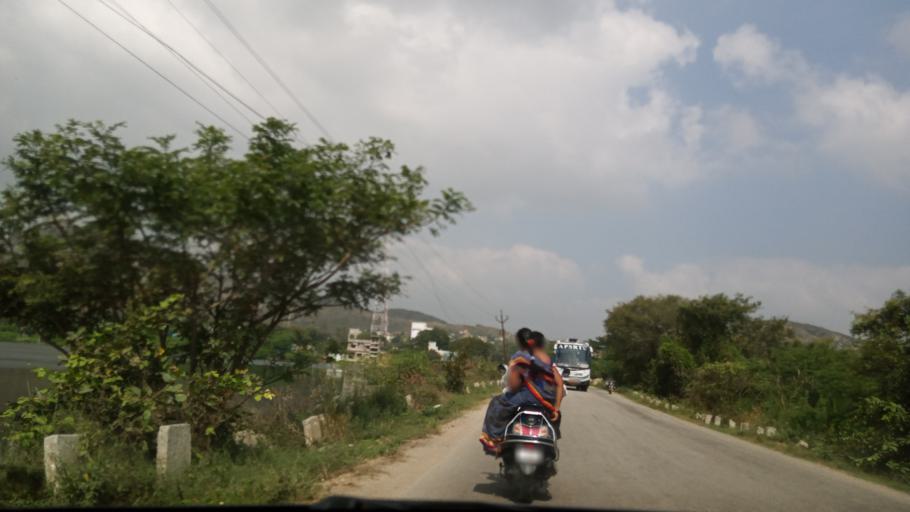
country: IN
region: Andhra Pradesh
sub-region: Chittoor
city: Madanapalle
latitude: 13.5760
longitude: 78.5191
